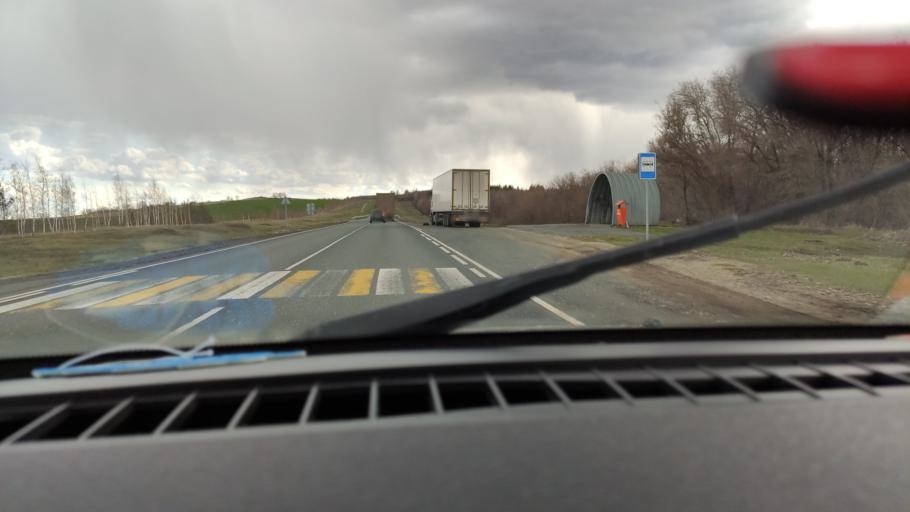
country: RU
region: Saratov
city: Balakovo
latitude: 52.1729
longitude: 47.8328
